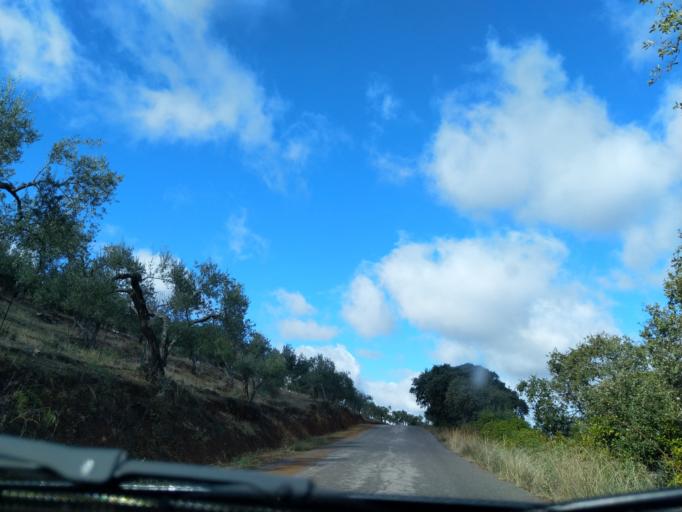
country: ES
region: Extremadura
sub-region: Provincia de Badajoz
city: Reina
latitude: 38.1273
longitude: -5.9216
